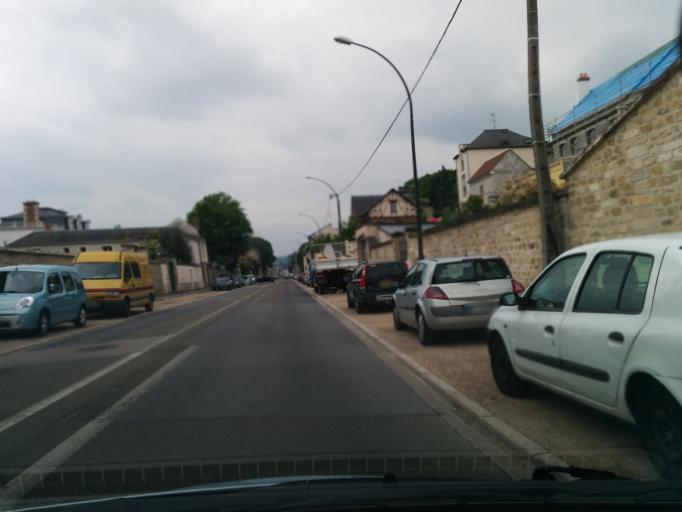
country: FR
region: Ile-de-France
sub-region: Departement des Yvelines
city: Meulan-en-Yvelines
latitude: 49.0065
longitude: 1.9209
